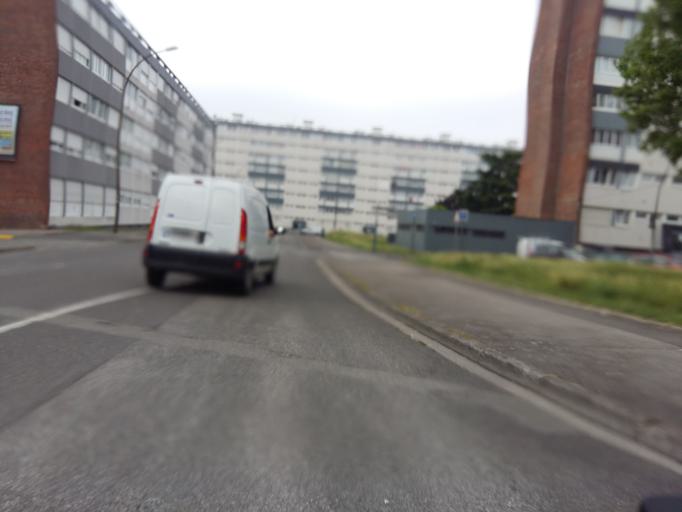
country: FR
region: Picardie
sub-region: Departement de la Somme
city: Amiens
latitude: 49.9079
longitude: 2.3005
